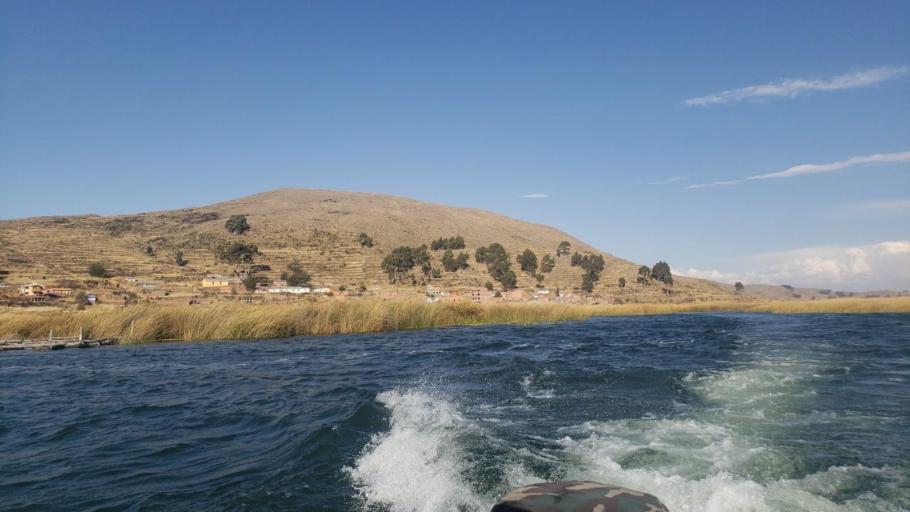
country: BO
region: La Paz
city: Huatajata
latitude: -16.3280
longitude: -68.7210
